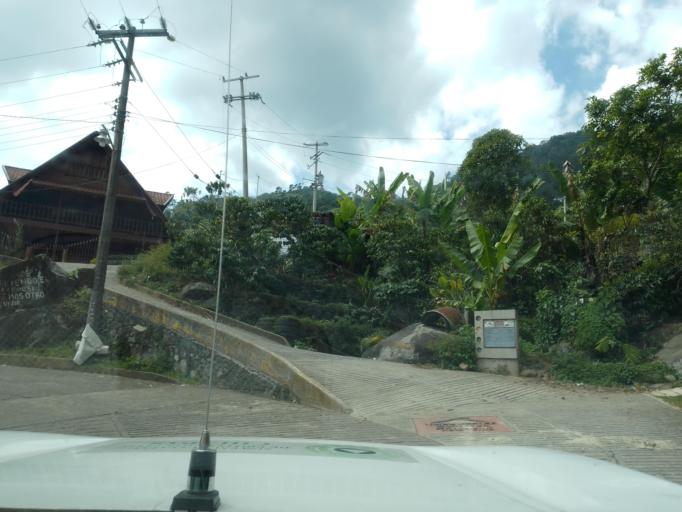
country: MX
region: Chiapas
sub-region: Union Juarez
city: Santo Domingo
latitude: 15.0606
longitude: -92.0942
